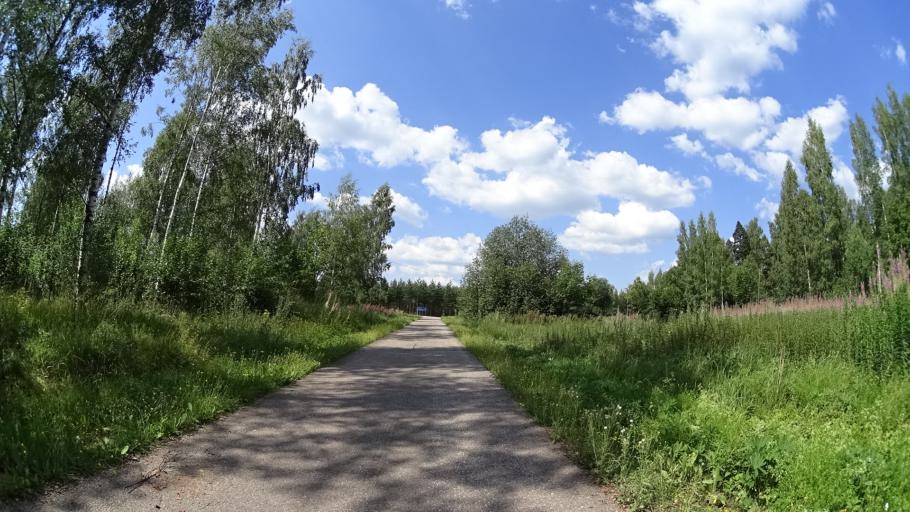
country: FI
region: Uusimaa
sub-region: Helsinki
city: Vantaa
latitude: 60.3423
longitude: 25.0047
